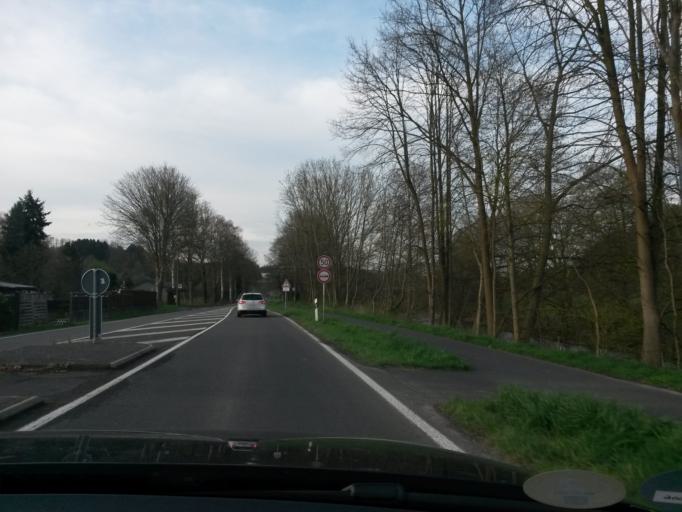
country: DE
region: North Rhine-Westphalia
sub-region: Regierungsbezirk Koln
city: Overath
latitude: 50.9092
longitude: 7.2658
